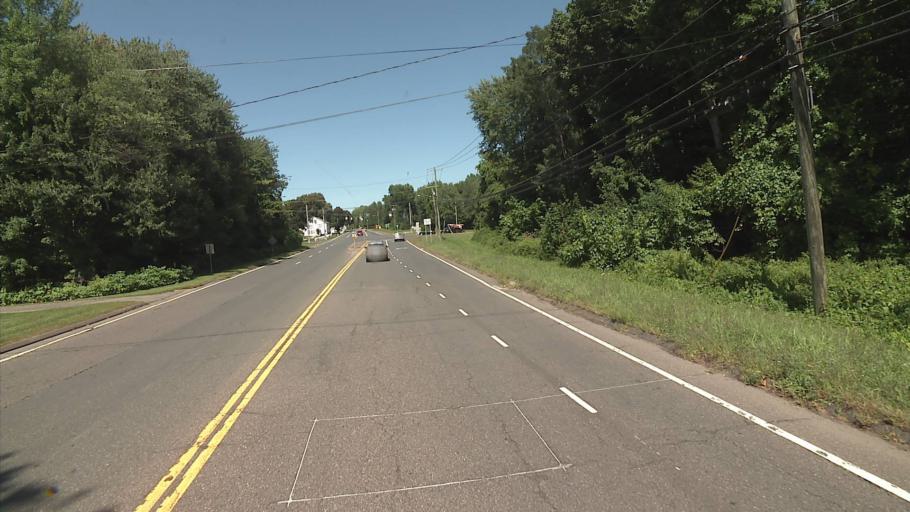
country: US
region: Connecticut
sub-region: Hartford County
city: Thompsonville
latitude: 41.9869
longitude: -72.6133
